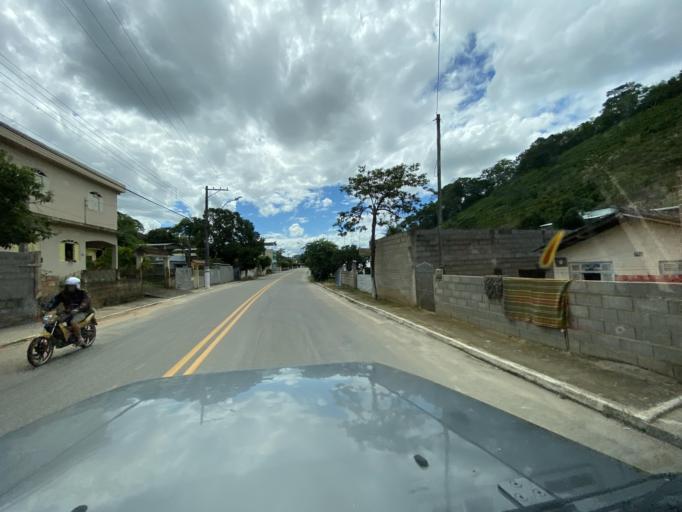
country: BR
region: Espirito Santo
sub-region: Jeronimo Monteiro
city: Jeronimo Monteiro
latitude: -20.7909
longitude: -41.3845
